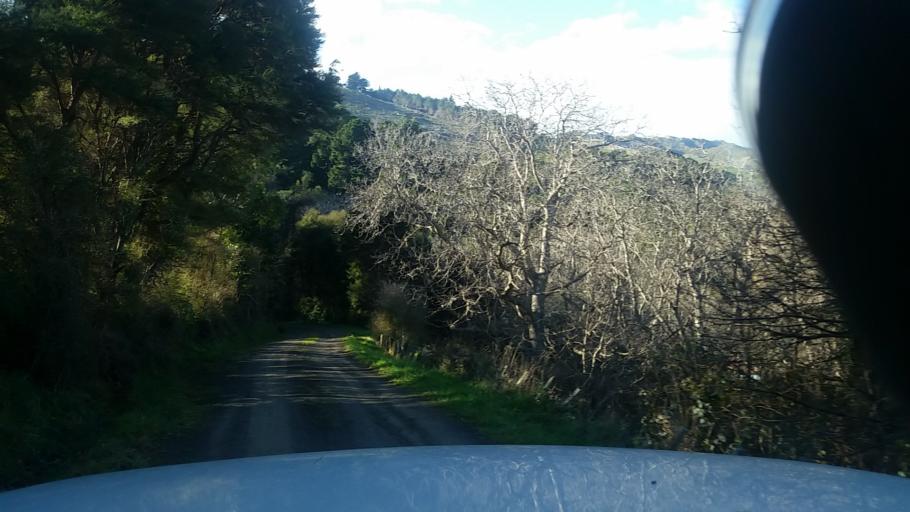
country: NZ
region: Canterbury
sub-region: Christchurch City
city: Christchurch
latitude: -43.7750
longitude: 172.9802
